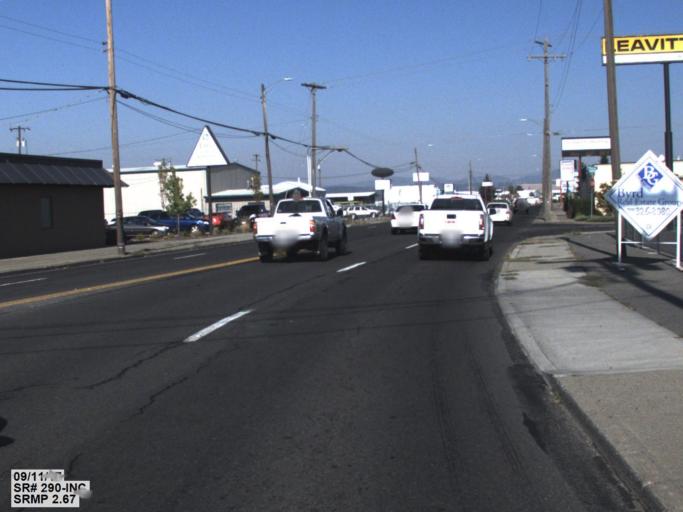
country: US
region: Washington
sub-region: Spokane County
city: Spokane
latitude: 47.6693
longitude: -117.3582
